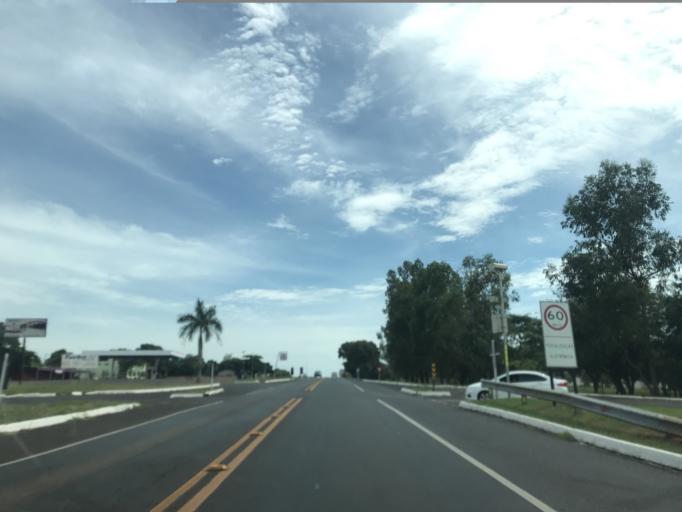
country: BR
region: Sao Paulo
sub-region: Nova Granada
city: Nova Granada
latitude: -20.2915
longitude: -49.2026
